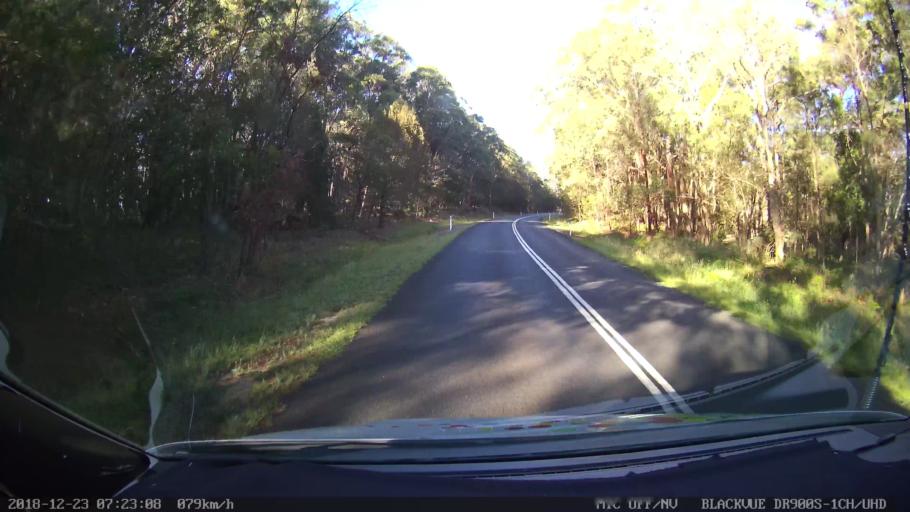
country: AU
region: New South Wales
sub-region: Armidale Dumaresq
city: Enmore
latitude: -30.5056
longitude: 152.2398
